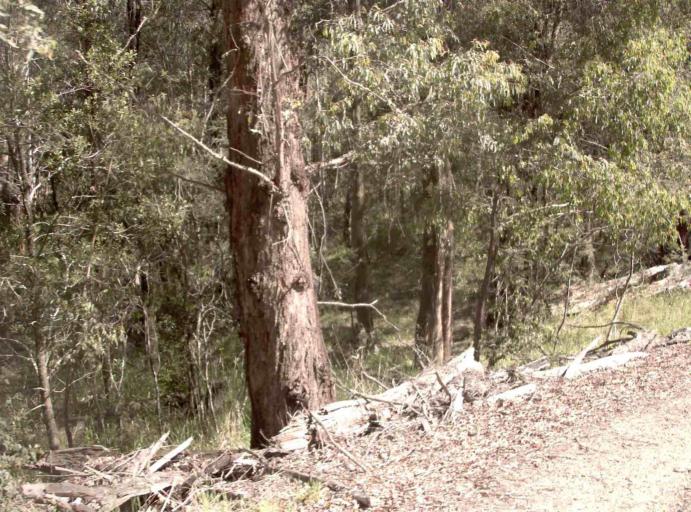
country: AU
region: New South Wales
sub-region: Bombala
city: Bombala
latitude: -37.1613
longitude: 148.7206
